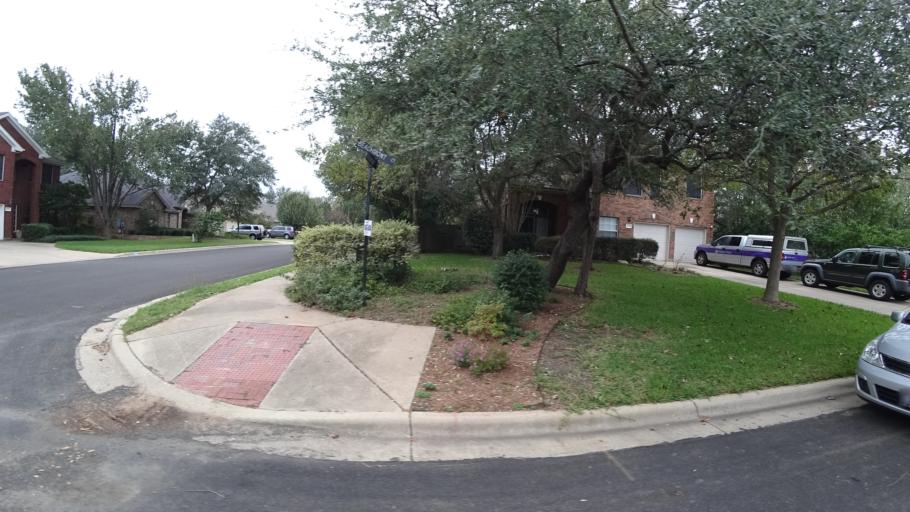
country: US
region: Texas
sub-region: Travis County
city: Shady Hollow
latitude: 30.1859
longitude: -97.8844
